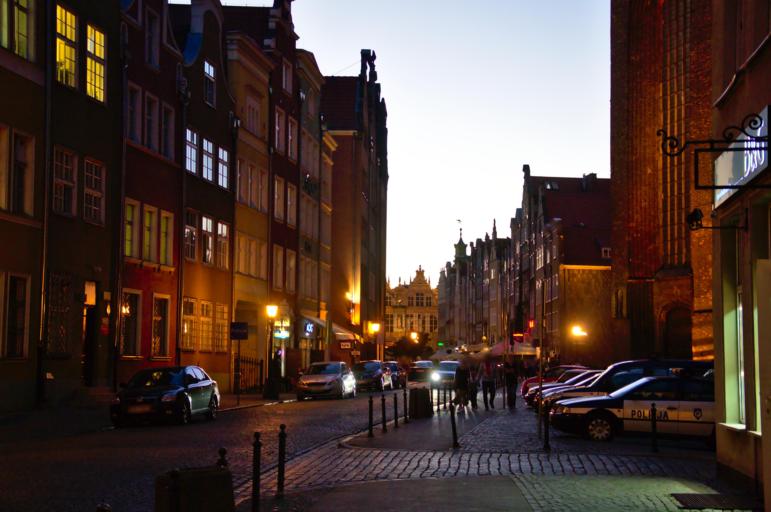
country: PL
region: Pomeranian Voivodeship
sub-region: Gdansk
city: Gdansk
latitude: 54.3493
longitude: 18.6533
